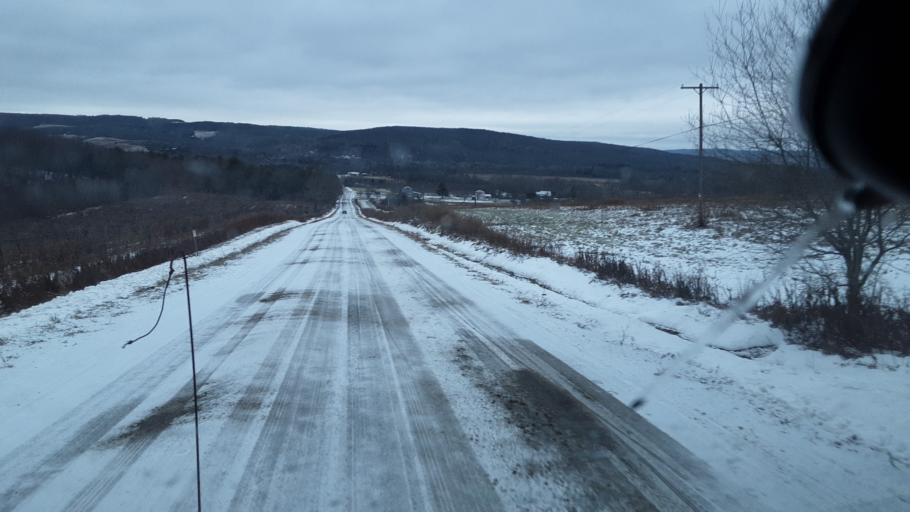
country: US
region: New York
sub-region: Allegany County
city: Friendship
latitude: 42.2871
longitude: -78.1623
